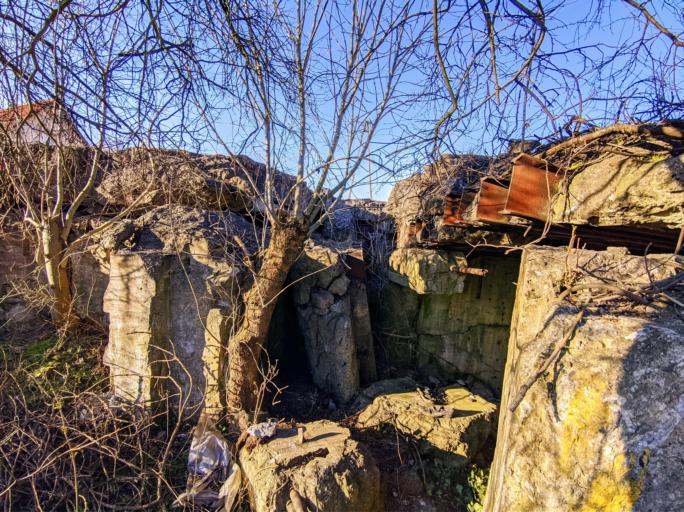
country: PL
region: Lubusz
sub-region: Powiat swiebodzinski
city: Lubrza
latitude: 52.2663
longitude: 15.3938
